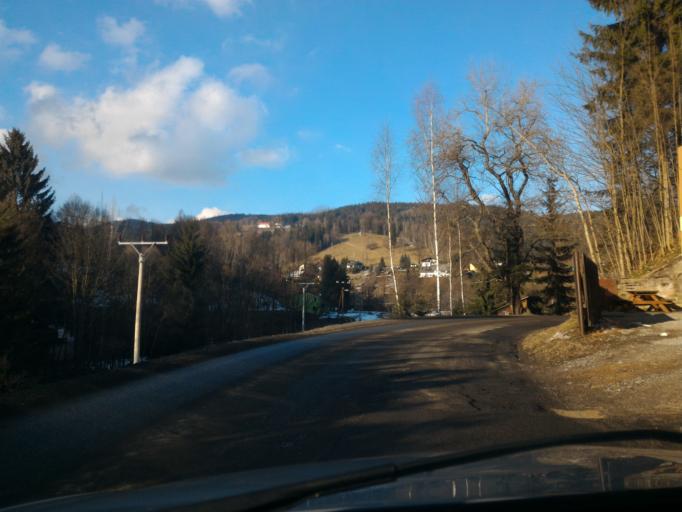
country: CZ
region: Liberecky
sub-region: Okres Jablonec nad Nisou
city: Smrzovka
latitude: 50.7594
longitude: 15.2686
